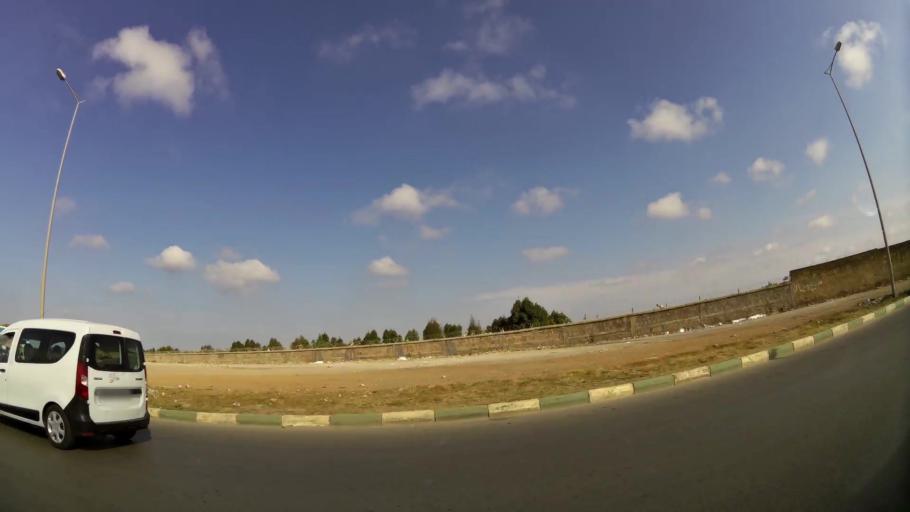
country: MA
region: Rabat-Sale-Zemmour-Zaer
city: Sale
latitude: 34.0593
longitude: -6.7690
